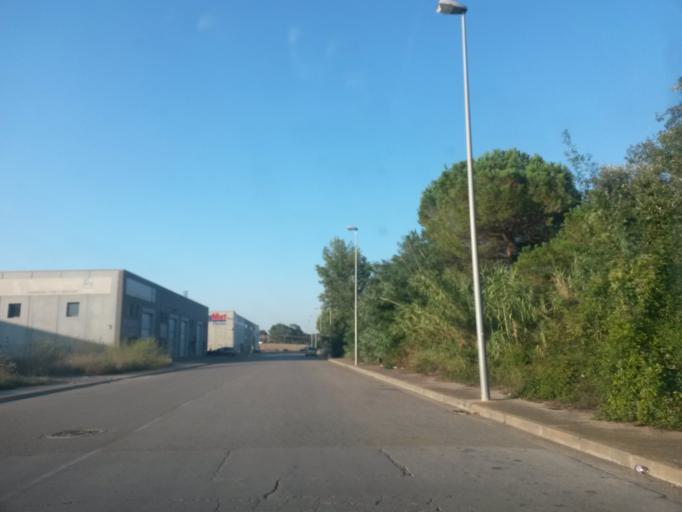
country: ES
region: Catalonia
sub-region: Provincia de Girona
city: Fornells de la Selva
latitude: 41.9342
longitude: 2.8034
